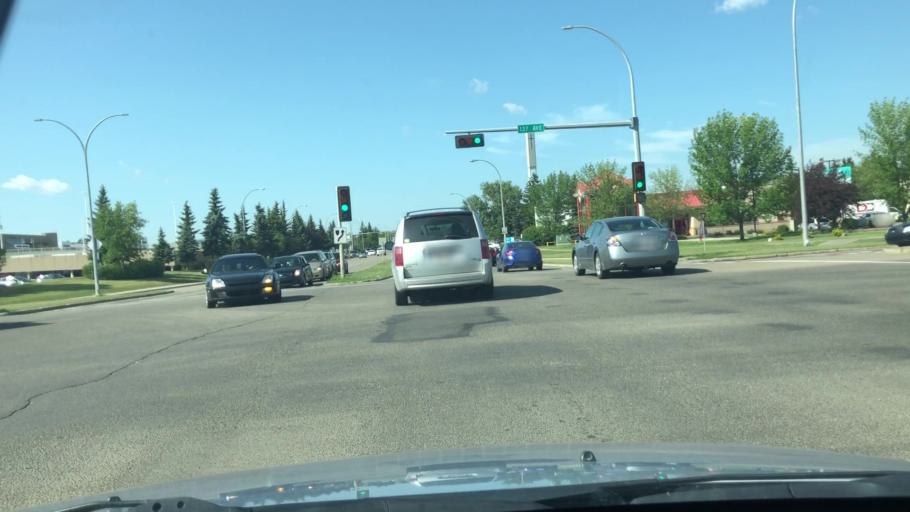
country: CA
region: Alberta
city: Edmonton
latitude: 53.5992
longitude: -113.4429
